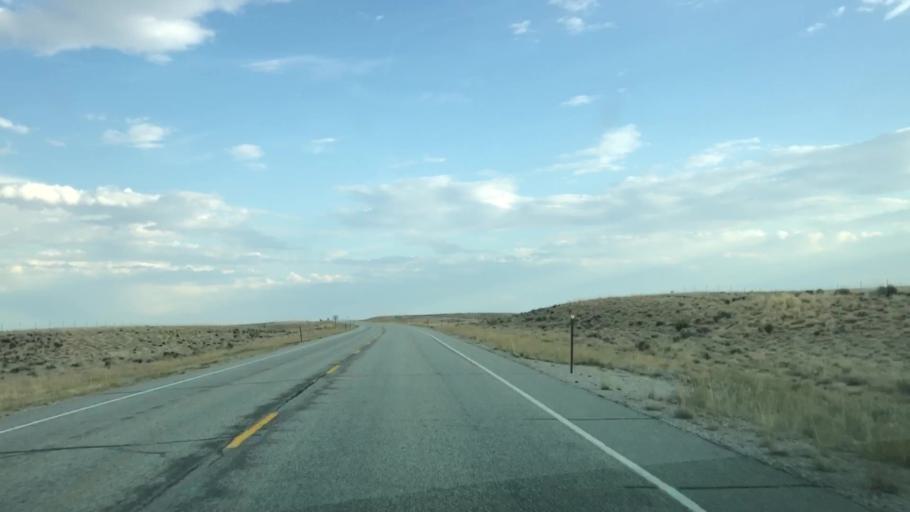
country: US
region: Wyoming
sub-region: Sweetwater County
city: North Rock Springs
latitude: 42.2823
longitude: -109.4865
